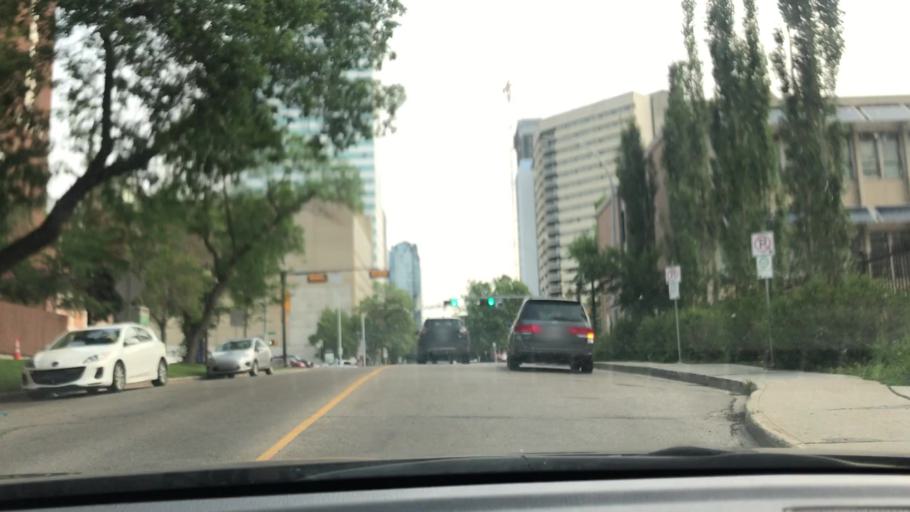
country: CA
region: Alberta
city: Edmonton
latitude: 53.5382
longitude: -113.4974
